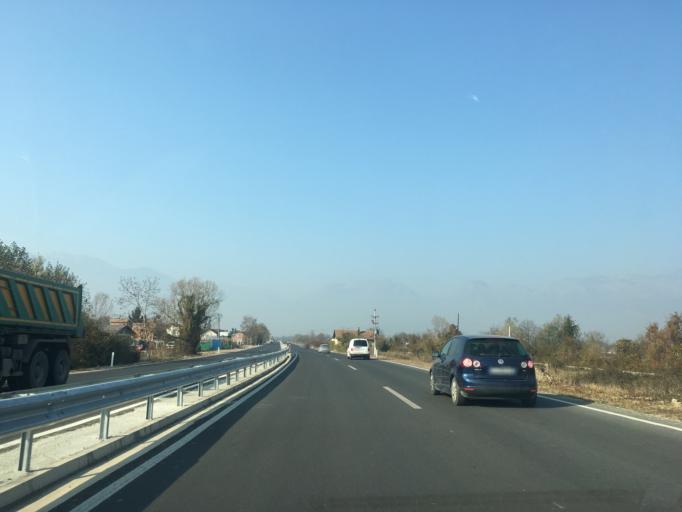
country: XK
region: Pec
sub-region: Komuna e Pejes
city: Dubova (Driloni)
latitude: 42.6582
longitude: 20.3832
